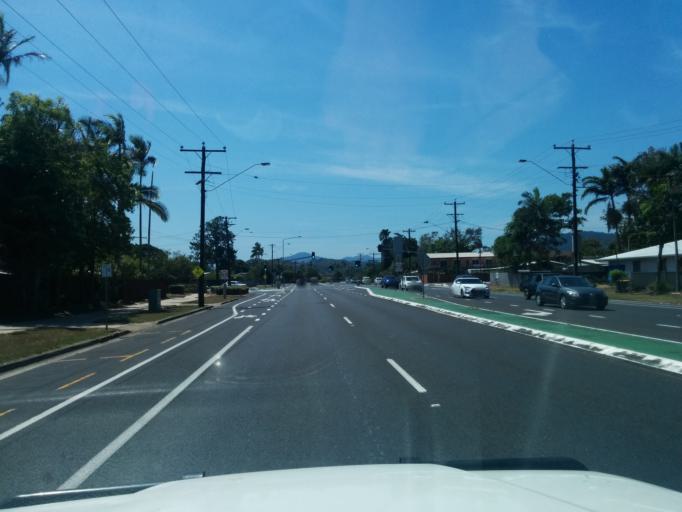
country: AU
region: Queensland
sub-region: Cairns
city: Woree
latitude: -16.9364
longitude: 145.7449
